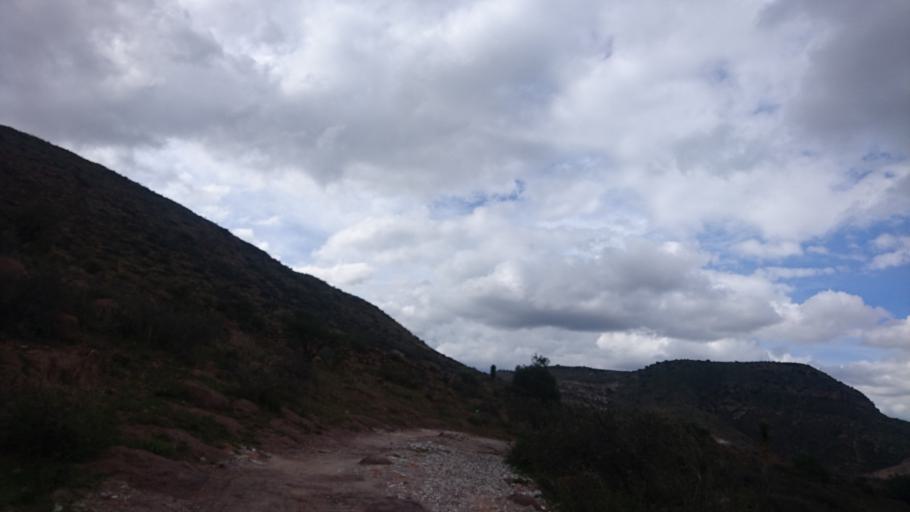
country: MX
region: San Luis Potosi
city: Escalerillas
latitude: 22.0837
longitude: -101.1012
